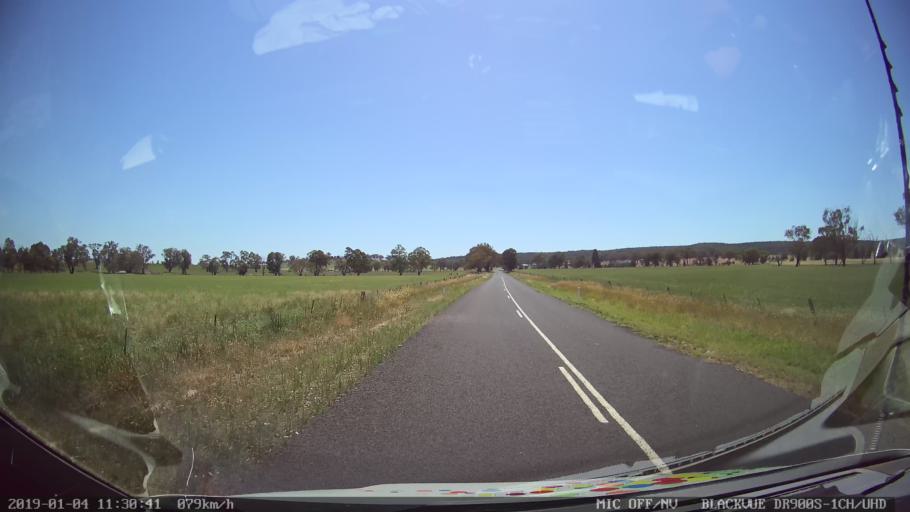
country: AU
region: New South Wales
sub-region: Cabonne
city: Molong
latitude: -33.0760
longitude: 148.7839
